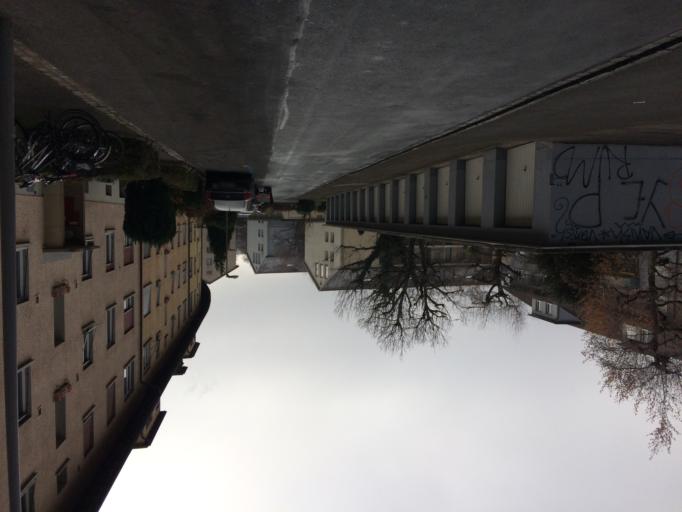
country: CH
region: Bern
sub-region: Bern-Mittelland District
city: Koniz
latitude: 46.9458
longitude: 7.4148
